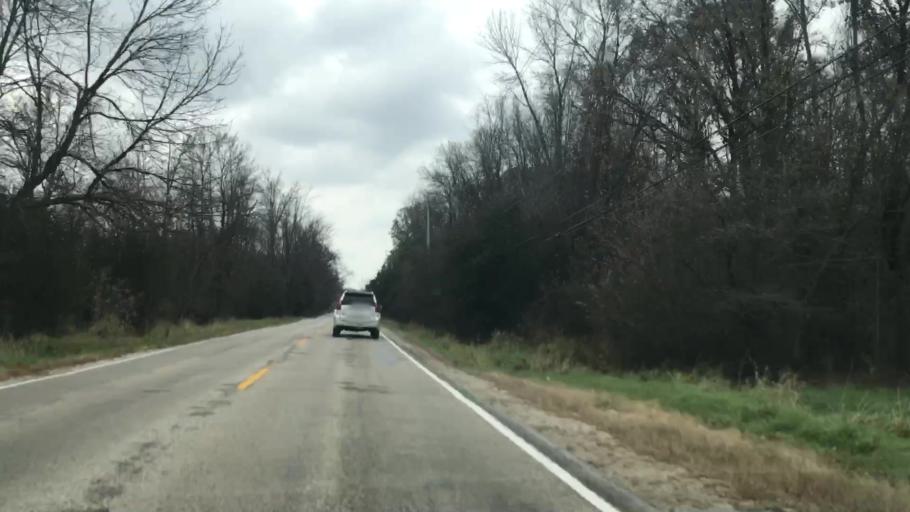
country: US
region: Wisconsin
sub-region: Waukesha County
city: Menomonee Falls
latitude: 43.2036
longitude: -88.1427
